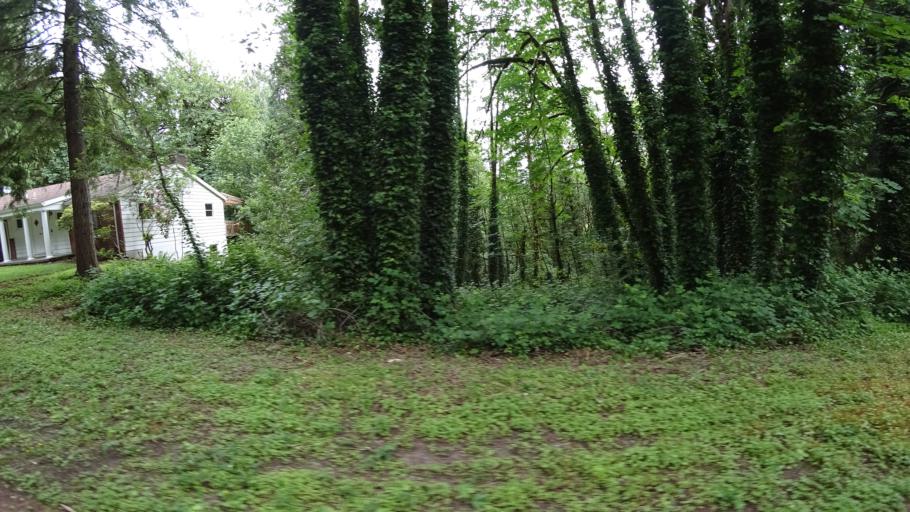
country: US
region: Oregon
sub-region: Clackamas County
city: Lake Oswego
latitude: 45.4284
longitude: -122.6731
